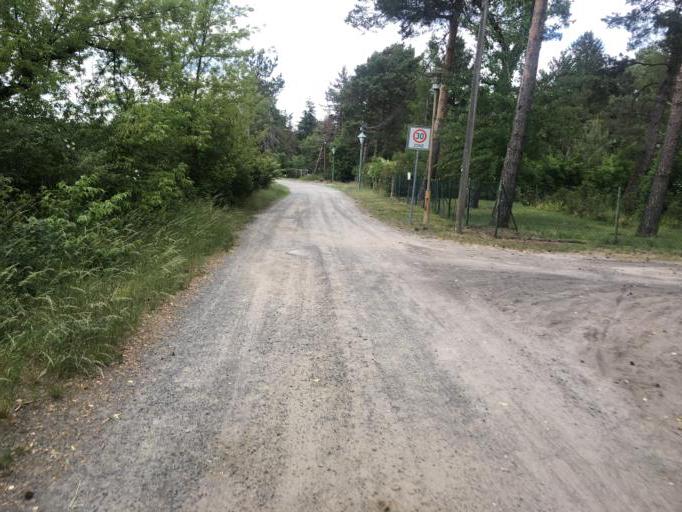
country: DE
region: Brandenburg
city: Bestensee
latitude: 52.2337
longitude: 13.7214
